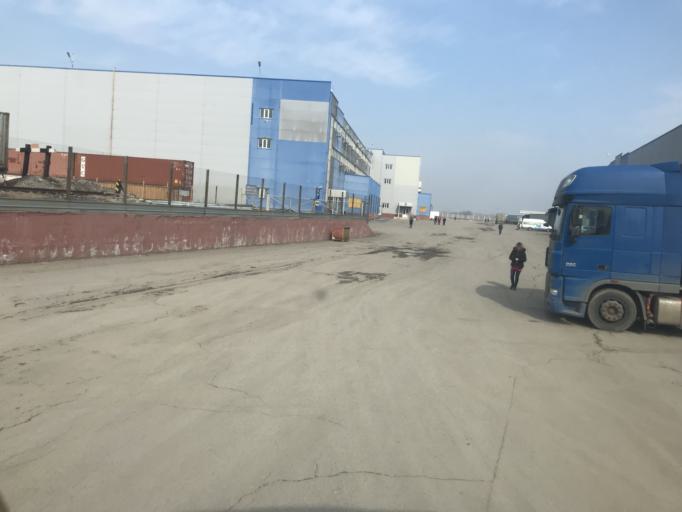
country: KZ
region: Almaty Oblysy
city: Pervomayskiy
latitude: 43.3617
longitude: 76.9760
